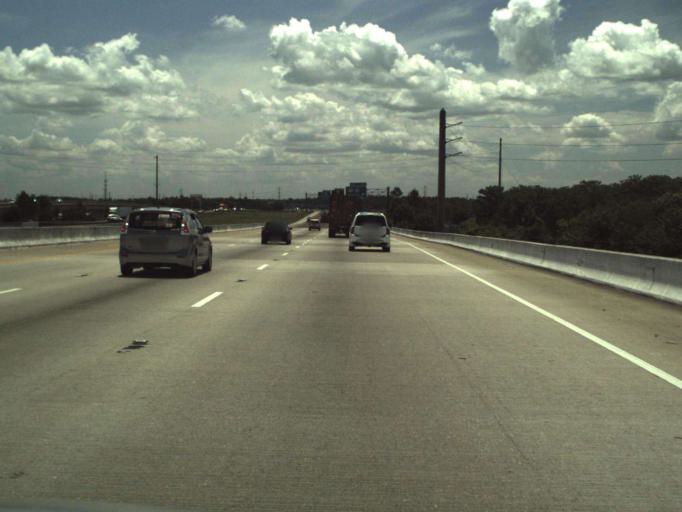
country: US
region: Florida
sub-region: Volusia County
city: DeBary
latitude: 28.8341
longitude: -81.3212
